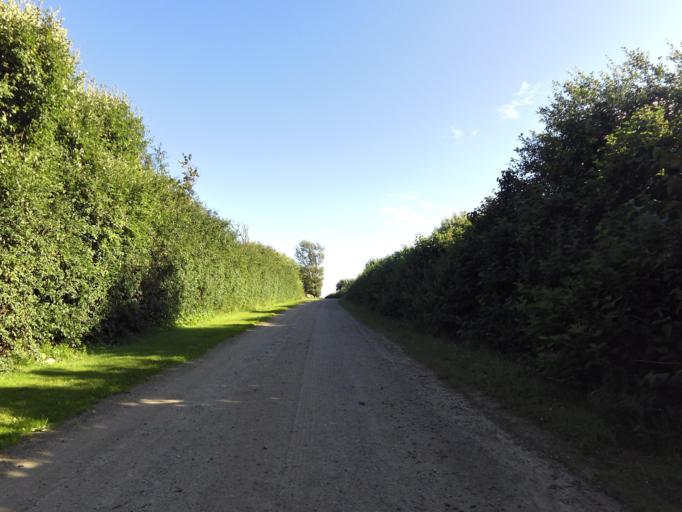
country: DK
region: South Denmark
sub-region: Vejen Kommune
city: Rodding
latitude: 55.3087
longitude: 9.1694
